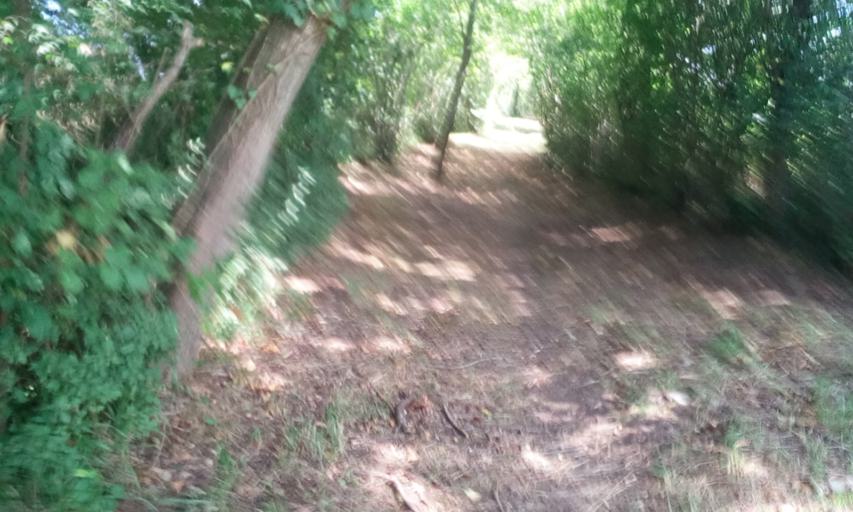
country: FR
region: Lower Normandy
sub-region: Departement du Calvados
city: Argences
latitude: 49.1460
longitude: -0.1579
